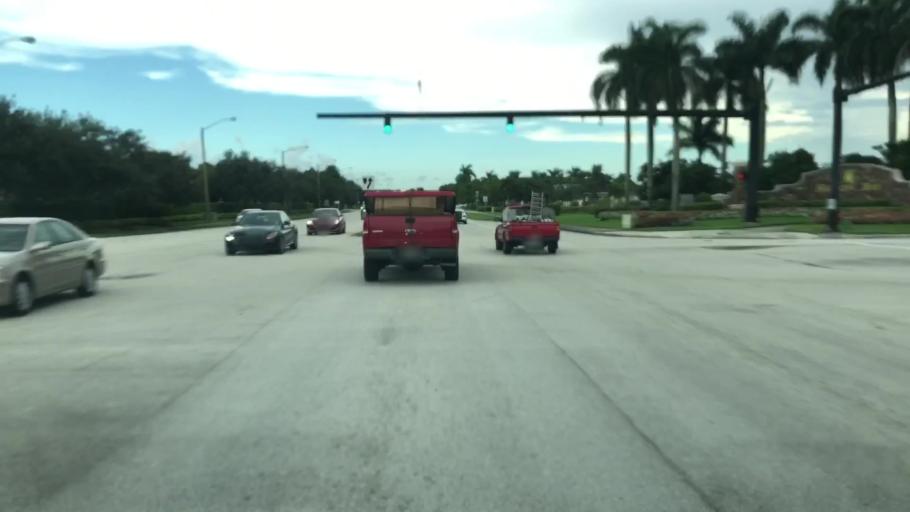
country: US
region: Florida
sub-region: Broward County
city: Coral Springs
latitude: 26.3089
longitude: -80.2789
